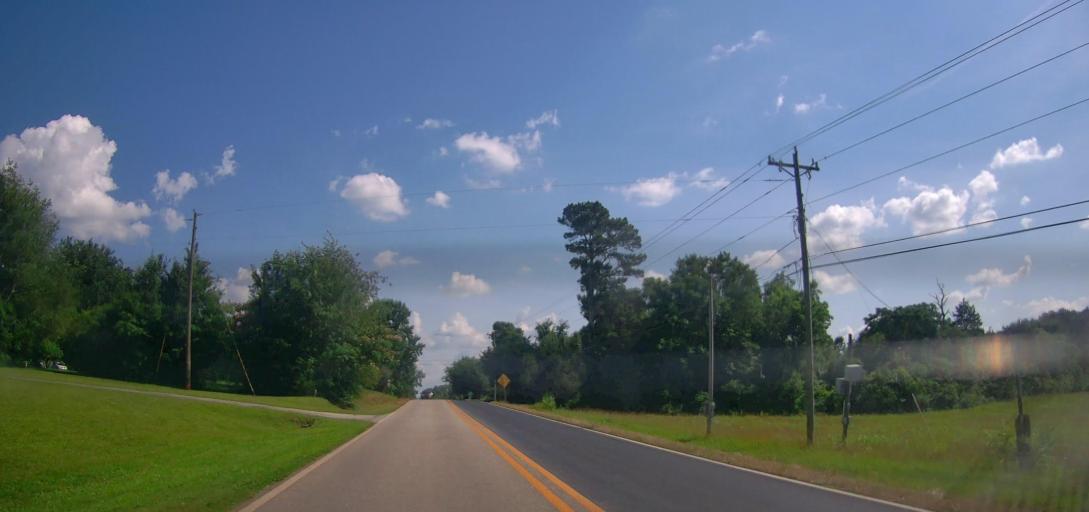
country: US
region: Georgia
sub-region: Spalding County
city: East Griffin
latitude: 33.2834
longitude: -84.1899
